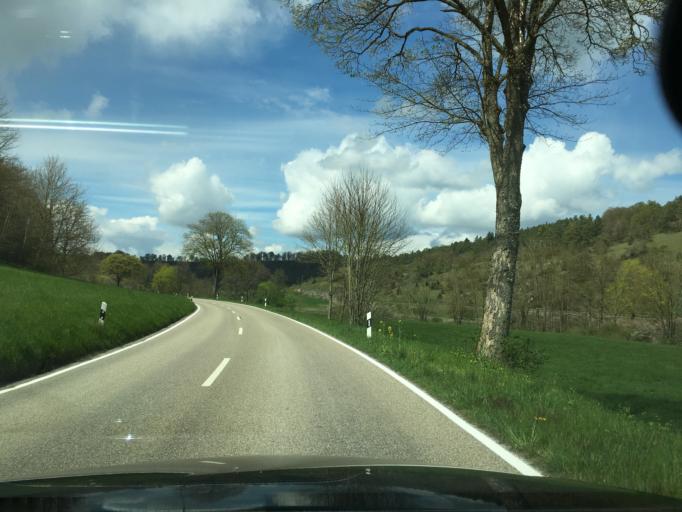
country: DE
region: Bavaria
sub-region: Upper Bavaria
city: Schernfeld
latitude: 48.8791
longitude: 11.0594
